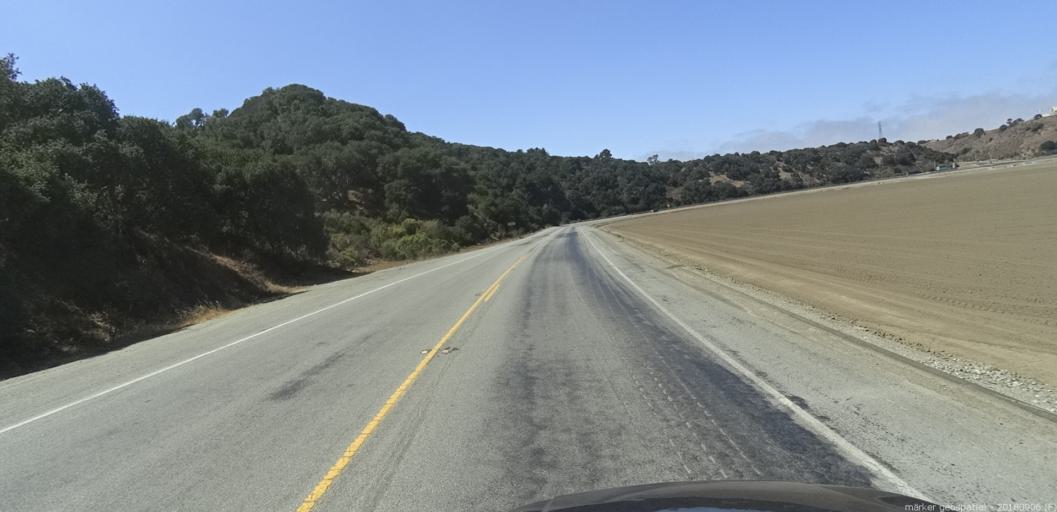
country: US
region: California
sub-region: Monterey County
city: Boronda
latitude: 36.6461
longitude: -121.7219
